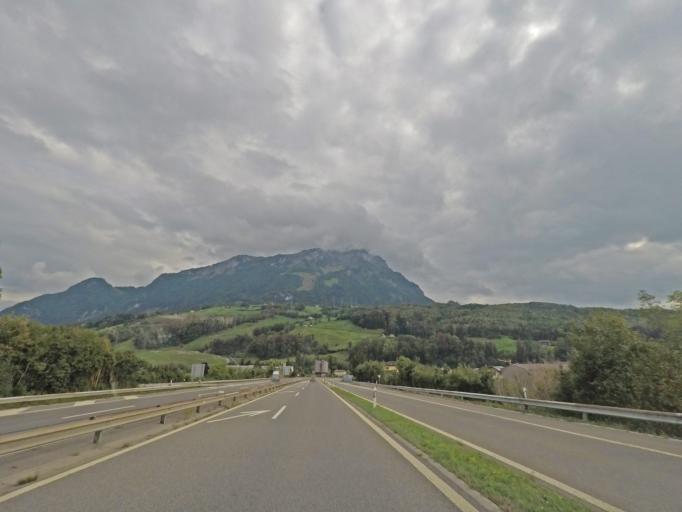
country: CH
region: Schwyz
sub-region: Bezirk Schwyz
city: Ingenbohl
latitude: 47.0036
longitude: 8.6211
